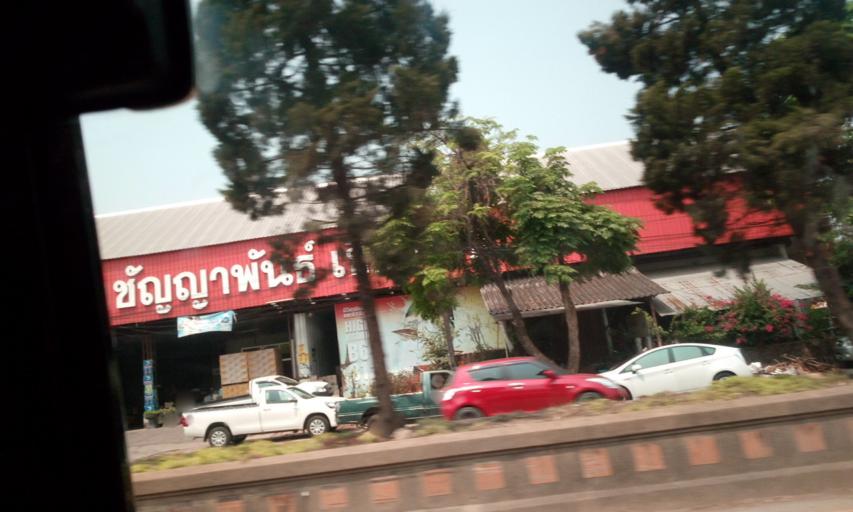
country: TH
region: Chiang Rai
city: Chiang Rai
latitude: 19.8776
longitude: 99.8307
